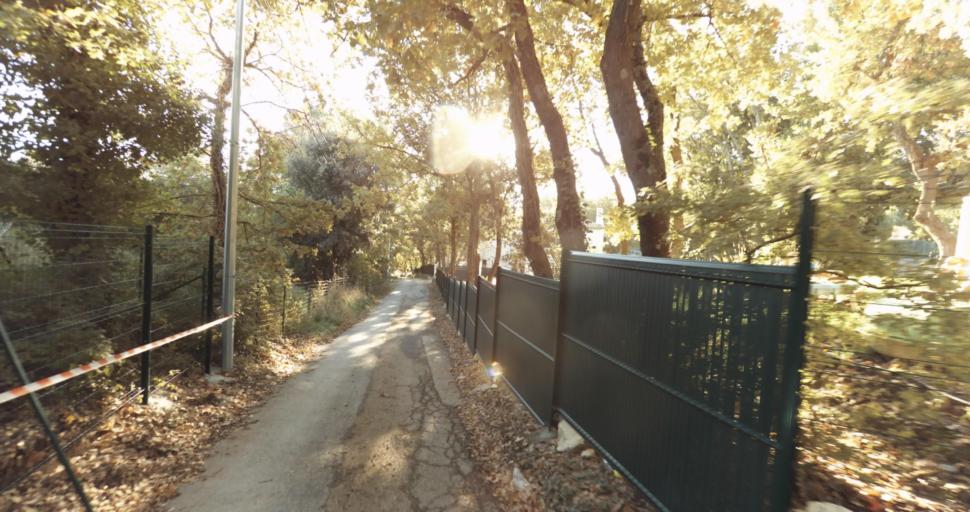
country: FR
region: Provence-Alpes-Cote d'Azur
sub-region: Departement des Bouches-du-Rhone
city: Venelles
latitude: 43.6102
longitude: 5.4775
